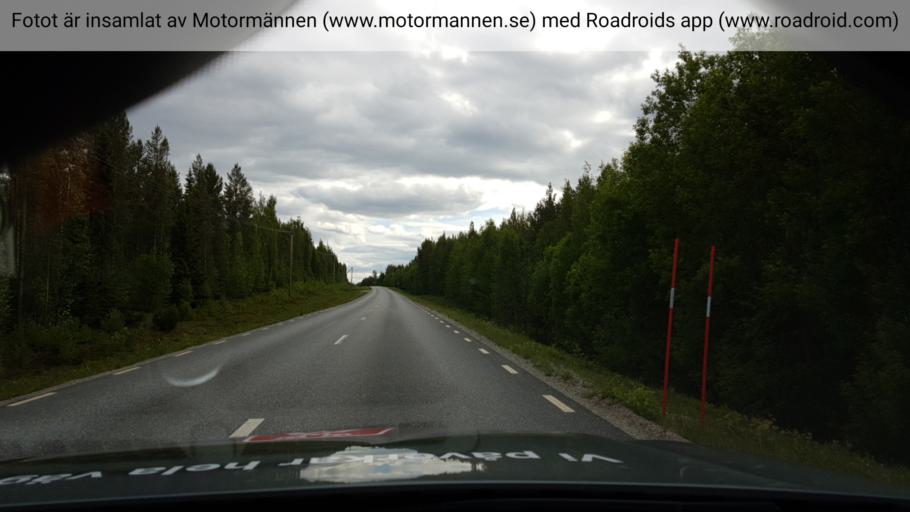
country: SE
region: Jaemtland
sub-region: Stroemsunds Kommun
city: Stroemsund
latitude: 63.9703
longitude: 15.4861
